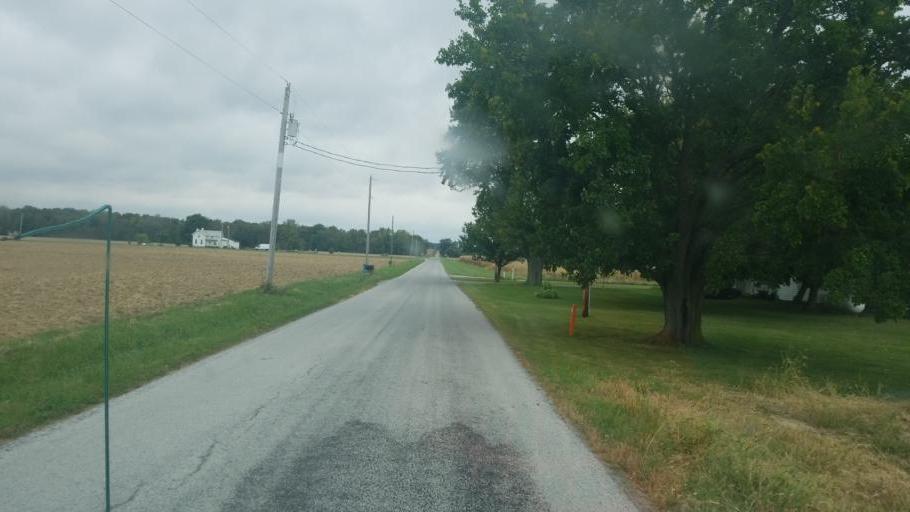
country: US
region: Ohio
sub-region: Seneca County
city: Fostoria
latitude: 41.0653
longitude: -83.4961
